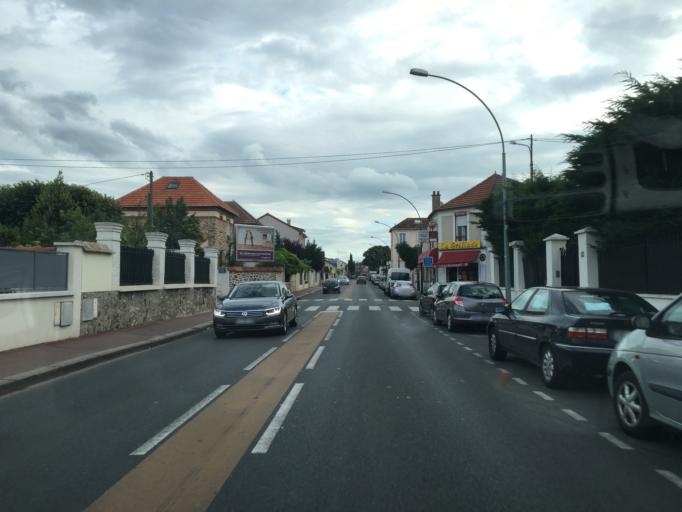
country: FR
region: Ile-de-France
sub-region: Departement du Val-de-Marne
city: Saint-Maur-des-Fosses
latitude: 48.7915
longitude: 2.4967
